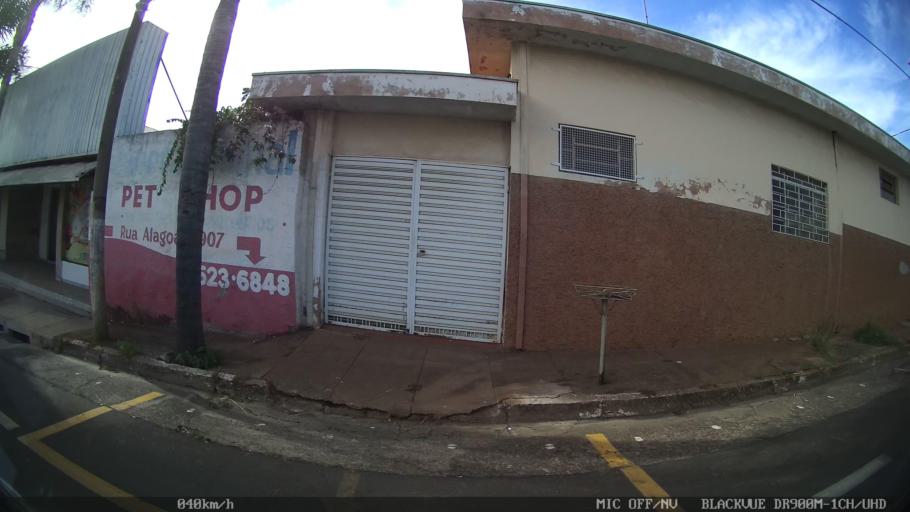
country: BR
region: Sao Paulo
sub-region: Catanduva
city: Catanduva
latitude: -21.1320
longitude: -48.9779
